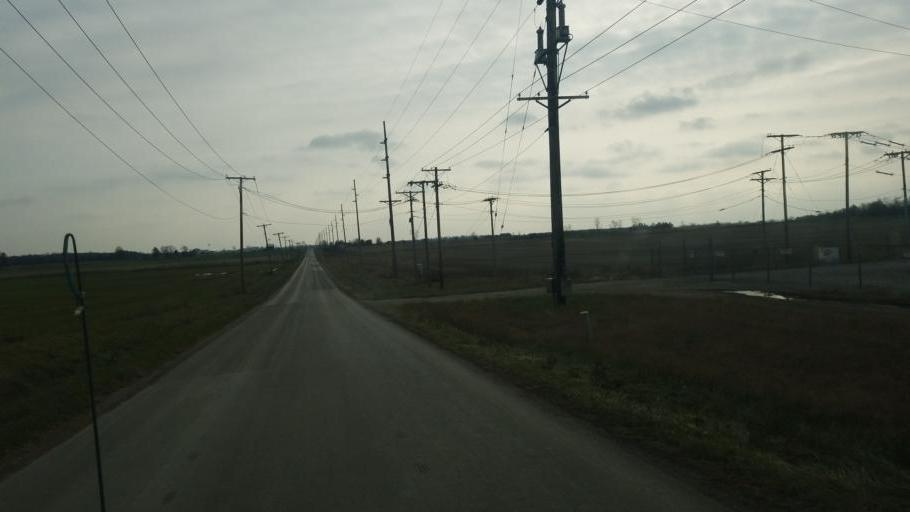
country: US
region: Indiana
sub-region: Adams County
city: Berne
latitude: 40.6429
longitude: -84.9643
